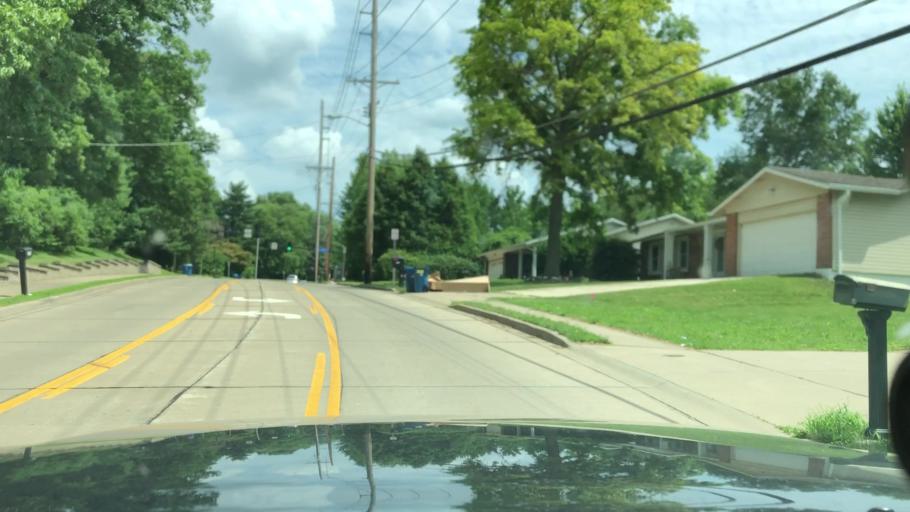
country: US
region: Missouri
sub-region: Saint Charles County
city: Saint Charles
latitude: 38.8069
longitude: -90.5102
